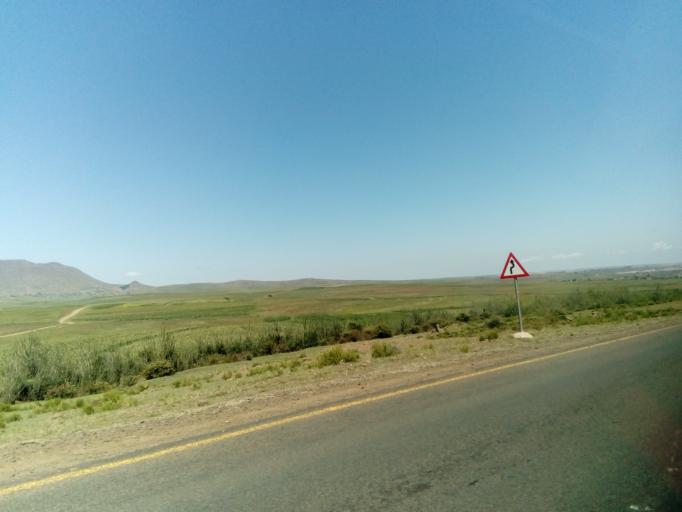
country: LS
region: Berea
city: Teyateyaneng
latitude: -29.2194
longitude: 27.8538
